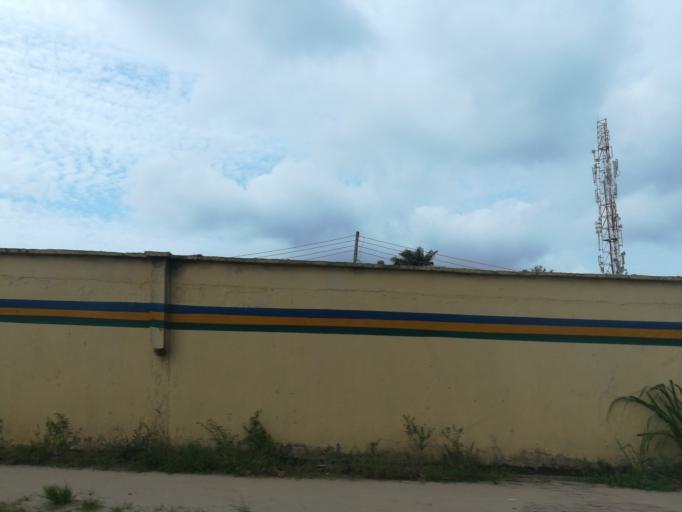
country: NG
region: Lagos
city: Ikeja
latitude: 6.5905
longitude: 3.3509
